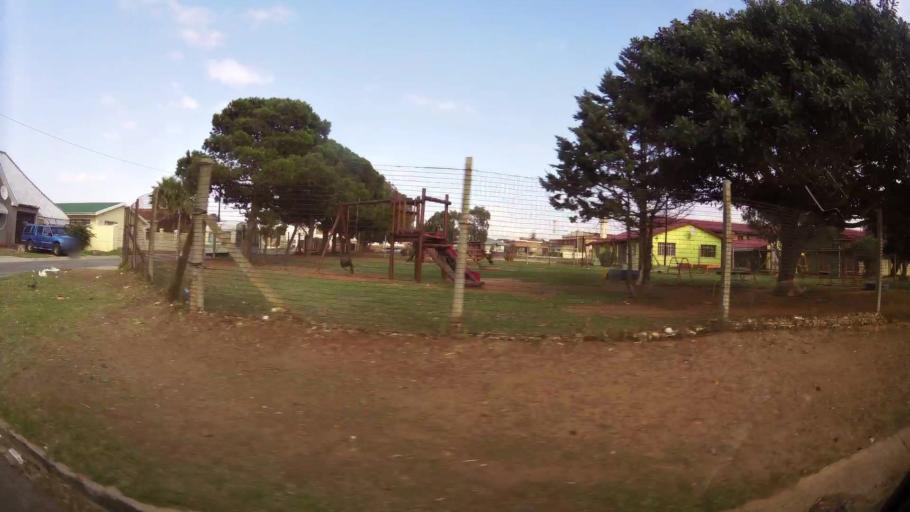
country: ZA
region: Eastern Cape
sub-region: Nelson Mandela Bay Metropolitan Municipality
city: Port Elizabeth
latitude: -33.9192
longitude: 25.5628
